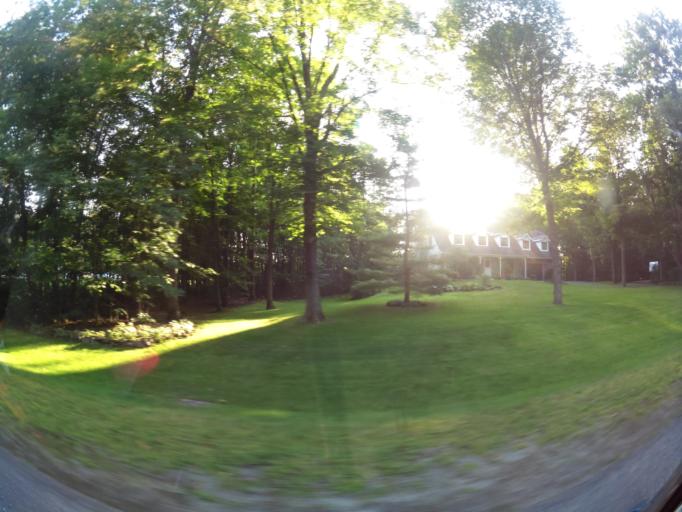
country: CA
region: Ontario
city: Clarence-Rockland
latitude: 45.5031
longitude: -75.4090
